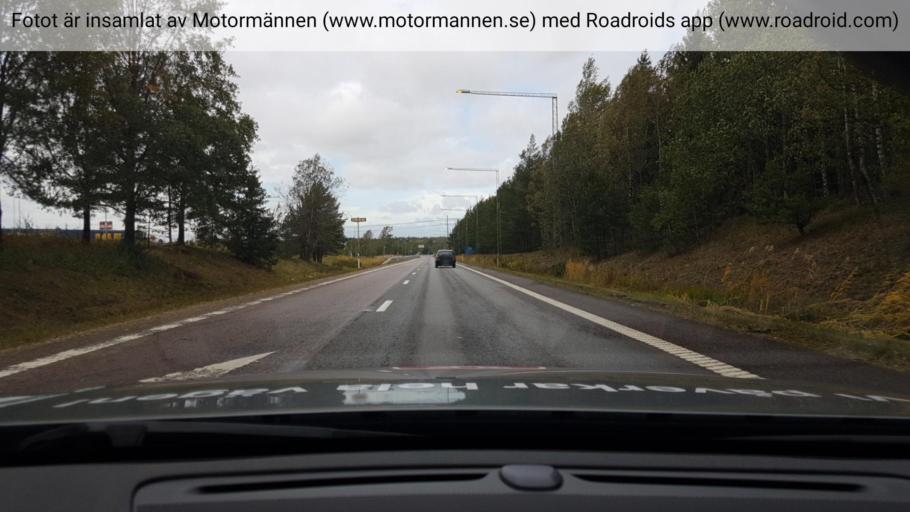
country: SE
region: Vaermland
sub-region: Hammaro Kommun
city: Skoghall
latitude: 59.3797
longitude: 13.4278
